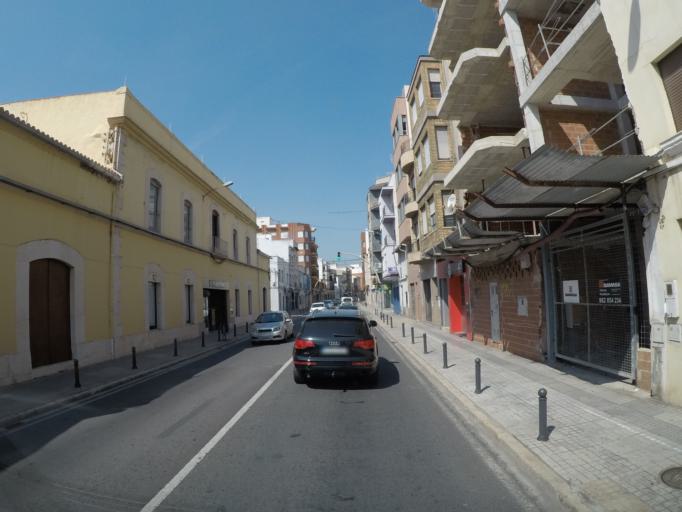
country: ES
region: Valencia
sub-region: Provincia de Valencia
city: Oliva
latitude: 38.9168
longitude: -0.1164
